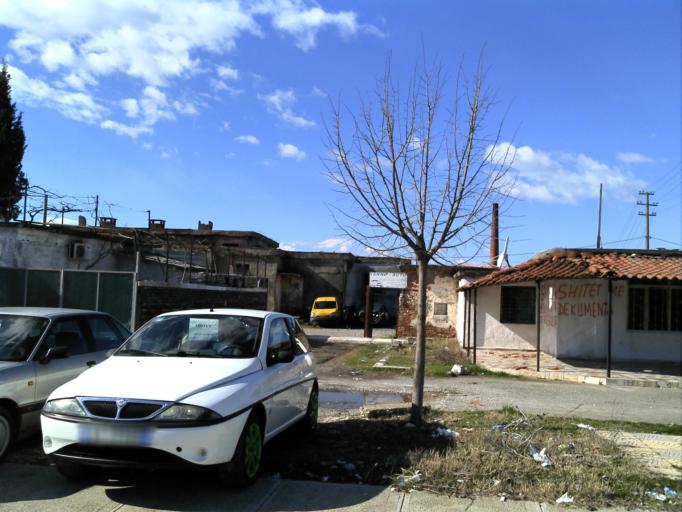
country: AL
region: Shkoder
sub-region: Rrethi i Shkodres
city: Shkoder
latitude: 42.0838
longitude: 19.5302
